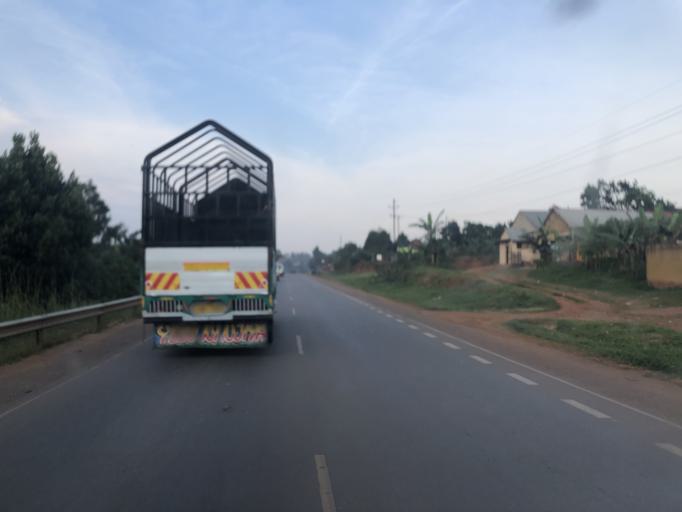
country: UG
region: Central Region
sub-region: Mpigi District
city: Mpigi
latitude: 0.2491
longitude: 32.3870
